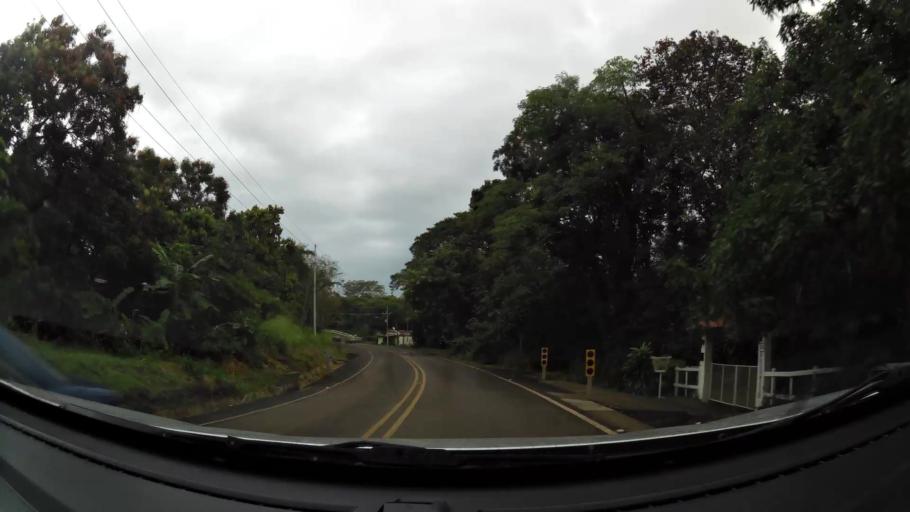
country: CR
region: Alajuela
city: Orotina
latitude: 9.9549
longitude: -84.5814
